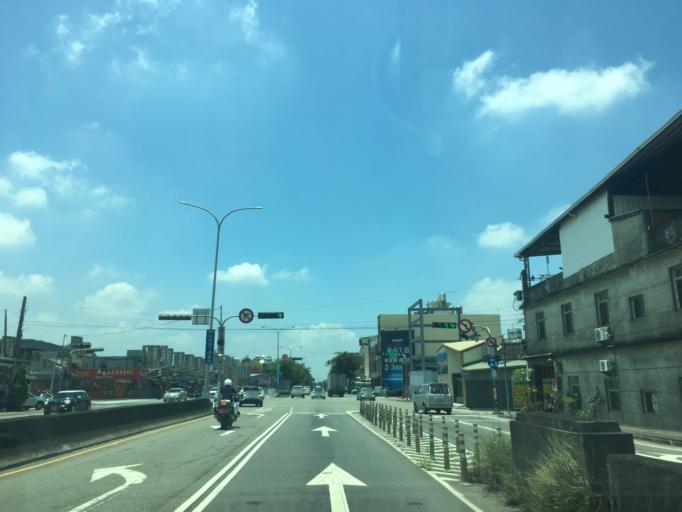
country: TW
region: Taiwan
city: Fengyuan
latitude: 24.2473
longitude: 120.7032
